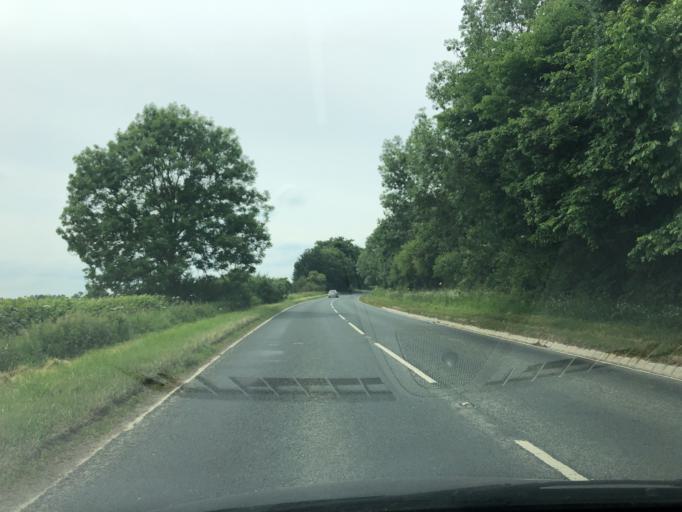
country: GB
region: England
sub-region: North Yorkshire
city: Great Habton
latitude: 54.2607
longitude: -0.8738
